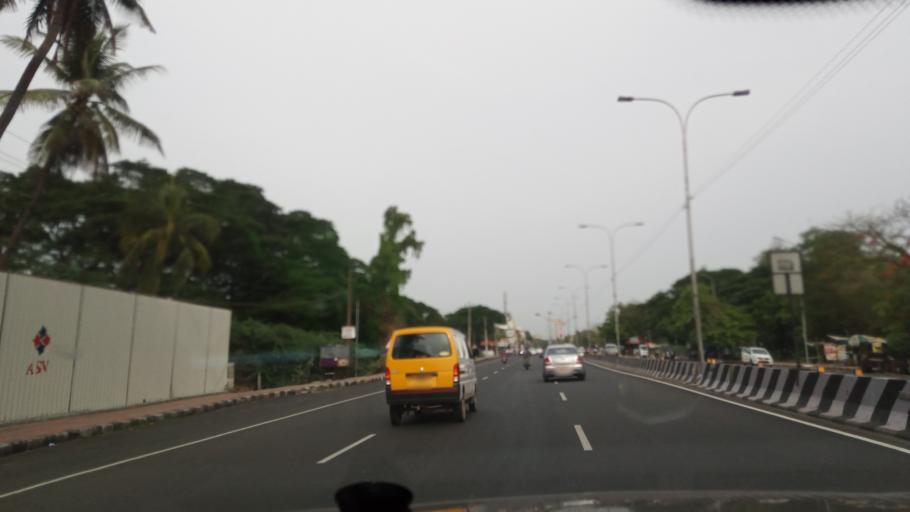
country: IN
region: Tamil Nadu
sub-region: Kancheepuram
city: Saint Thomas Mount
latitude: 13.0175
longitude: 80.1882
